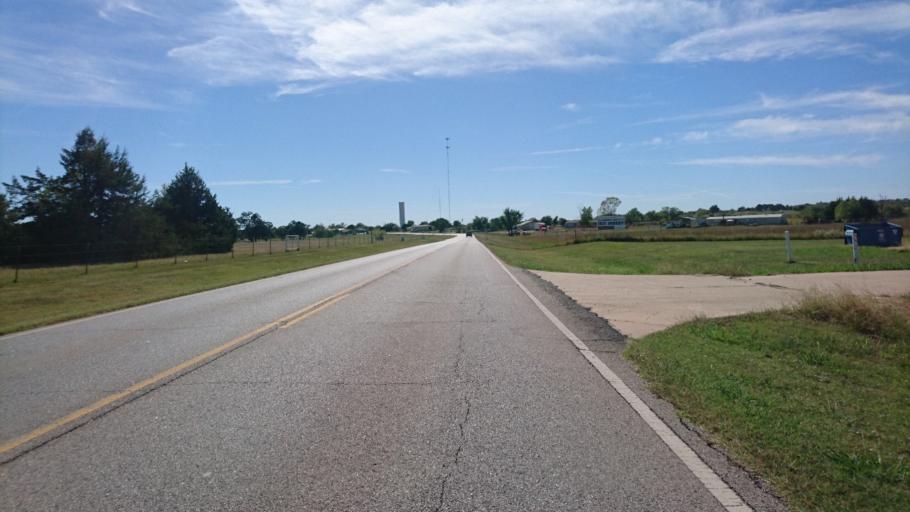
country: US
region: Oklahoma
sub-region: Lincoln County
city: Stroud
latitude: 35.7207
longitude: -96.7608
